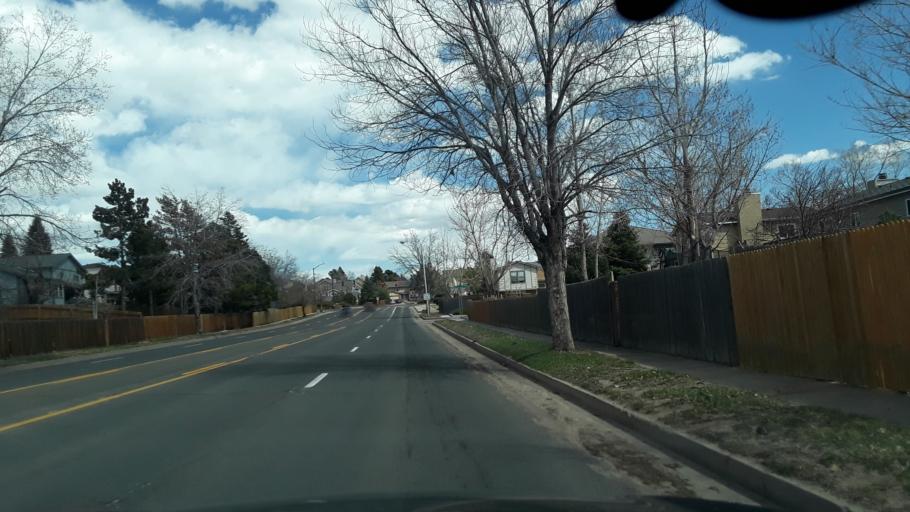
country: US
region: Colorado
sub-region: El Paso County
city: Black Forest
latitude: 38.9431
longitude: -104.7580
